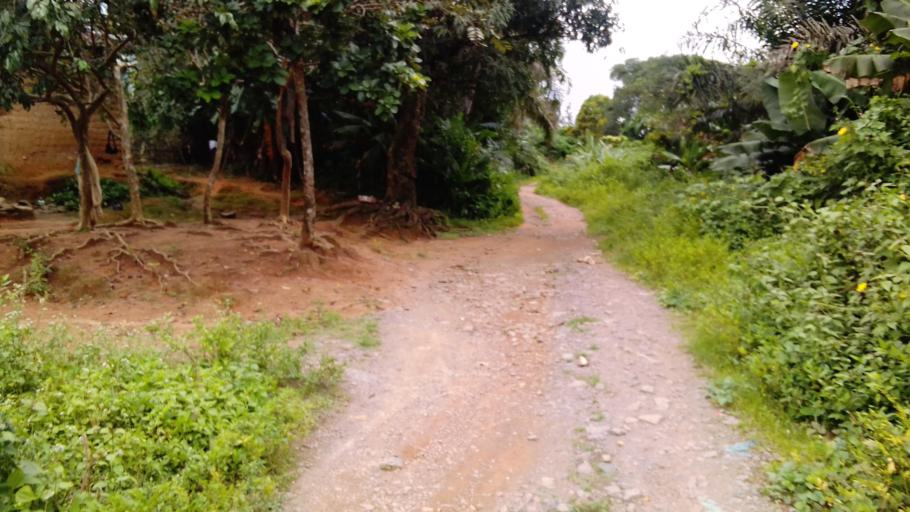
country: SL
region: Eastern Province
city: Koidu
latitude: 8.6583
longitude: -10.9333
